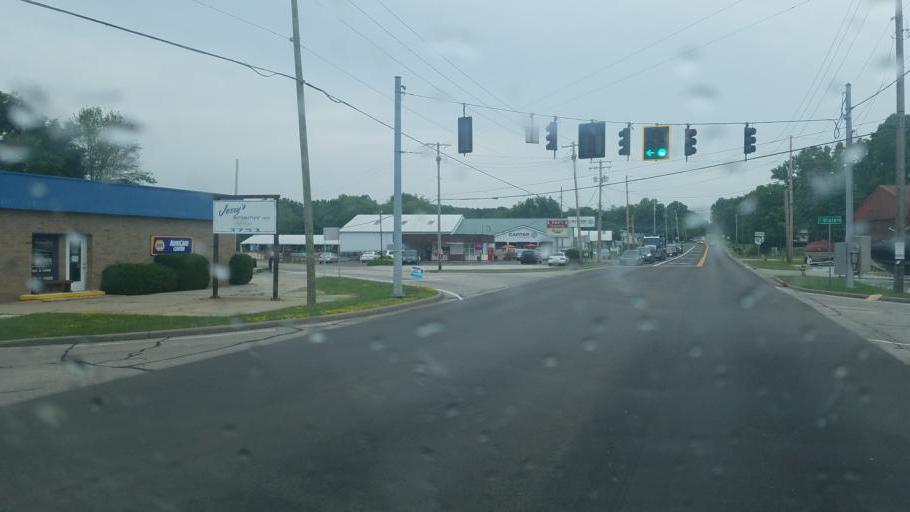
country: US
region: Ohio
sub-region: Summit County
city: Portage Lakes
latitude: 40.9981
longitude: -81.5572
